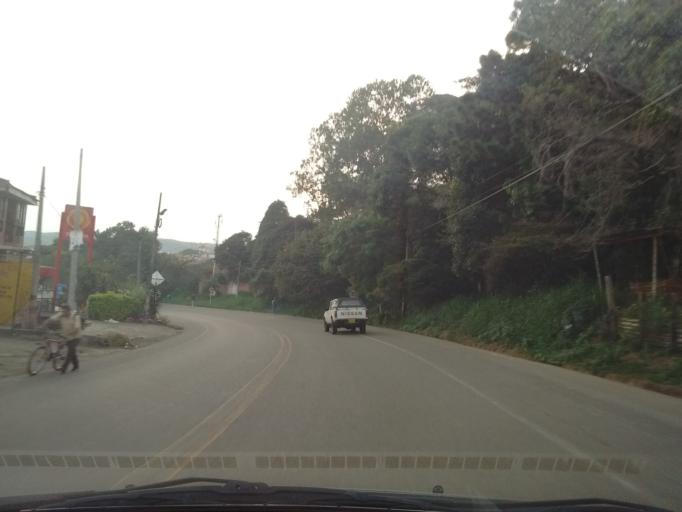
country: CO
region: Cauca
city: Santander de Quilichao
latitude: 3.0051
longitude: -76.4885
